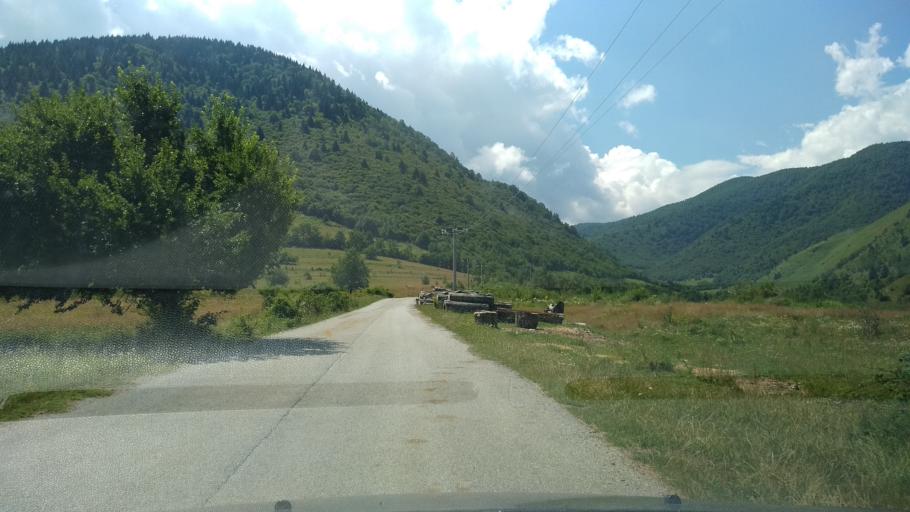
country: RO
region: Hunedoara
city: Salasu de Sus
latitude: 45.4763
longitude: 22.9080
